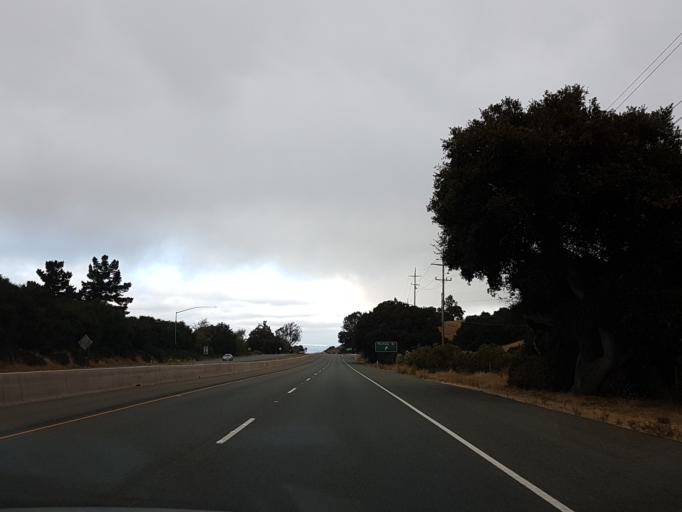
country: US
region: California
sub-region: Monterey County
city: Salinas
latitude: 36.6022
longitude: -121.6964
